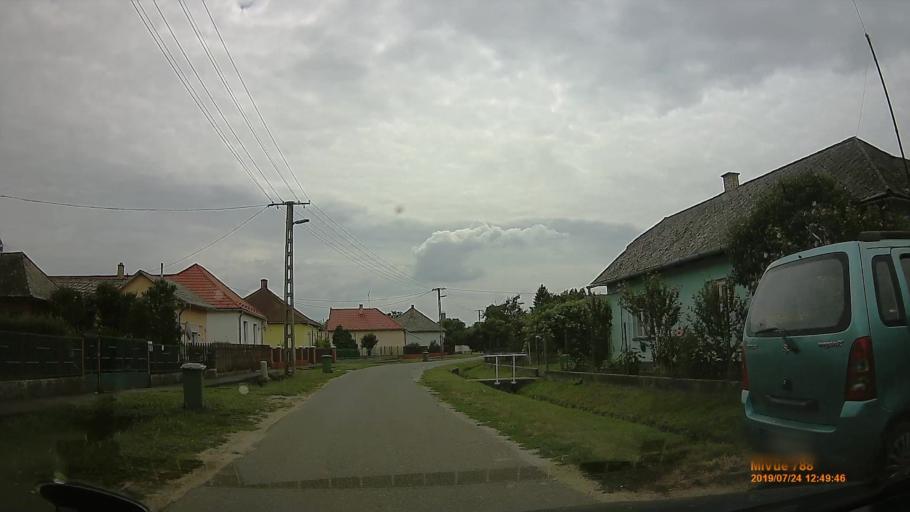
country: HU
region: Szabolcs-Szatmar-Bereg
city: Aranyosapati
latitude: 48.1886
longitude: 22.3131
